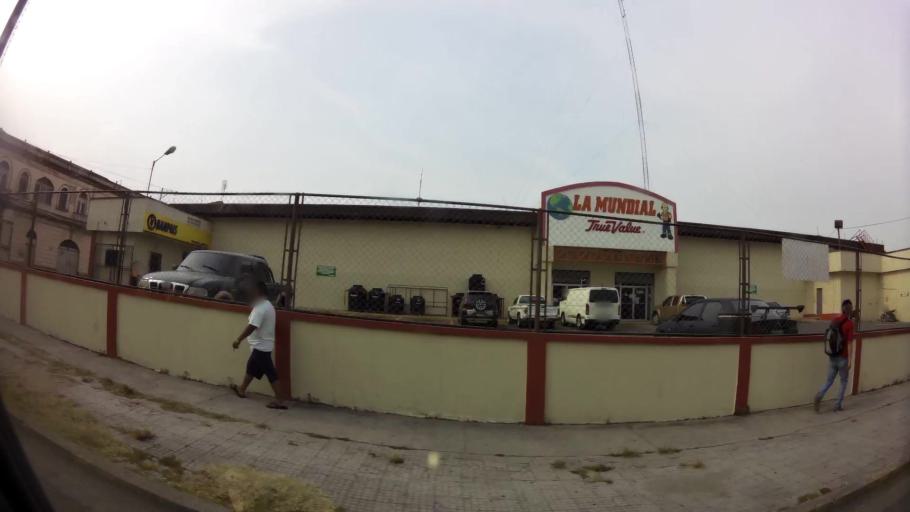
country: HN
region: Cortes
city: San Pedro Sula
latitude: 15.5009
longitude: -88.0281
